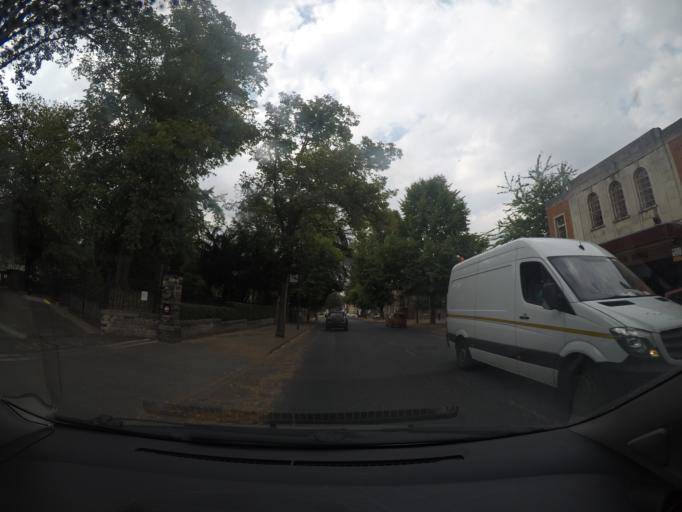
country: GB
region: England
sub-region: City of York
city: York
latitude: 53.9676
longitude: -1.0938
